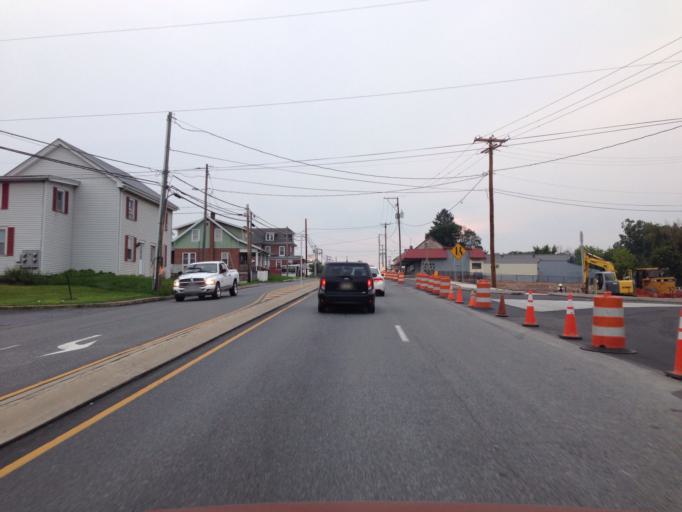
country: US
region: Pennsylvania
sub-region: Lancaster County
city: Ephrata
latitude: 40.1643
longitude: -76.1545
